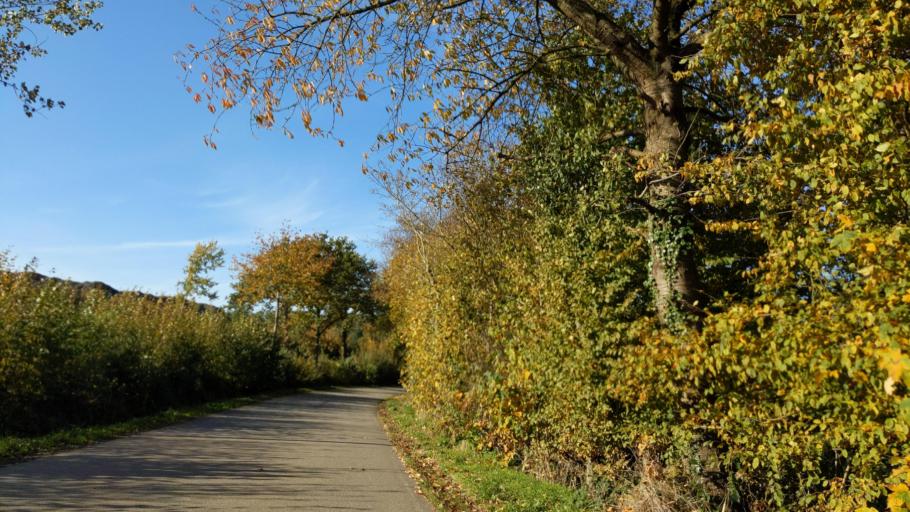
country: DE
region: Schleswig-Holstein
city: Kasseedorf
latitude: 54.1341
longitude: 10.7304
